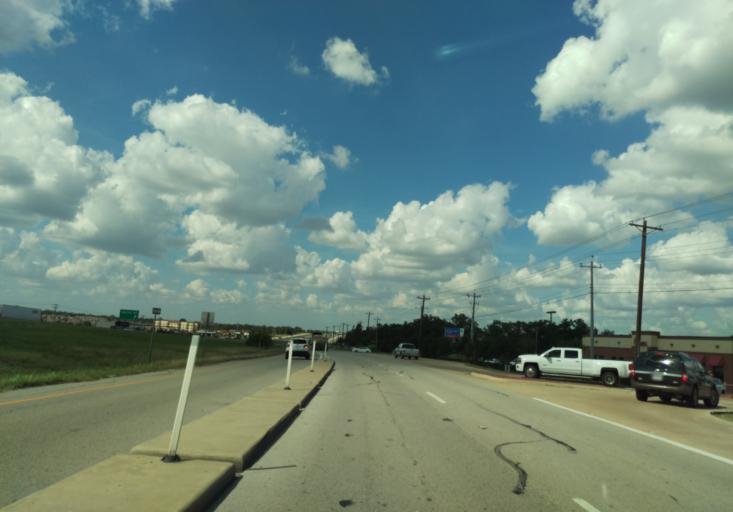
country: US
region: Texas
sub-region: Brazos County
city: College Station
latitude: 30.5609
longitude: -96.2588
